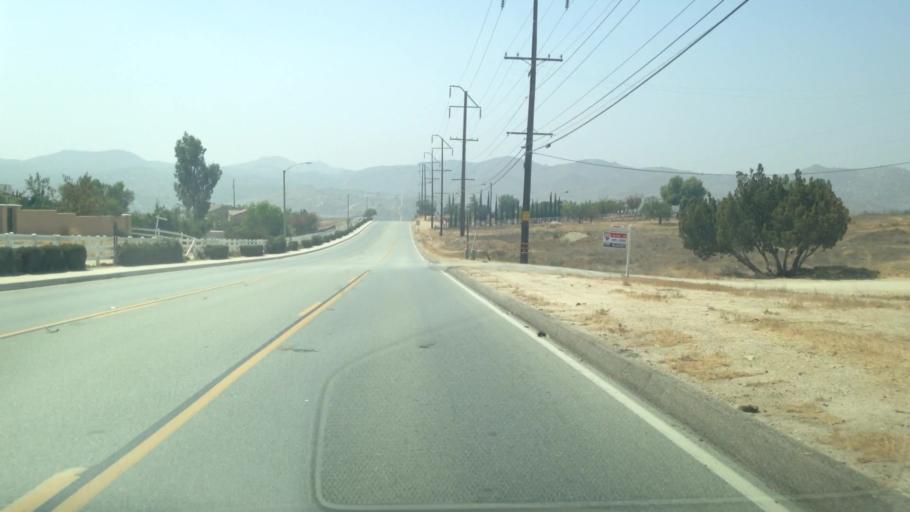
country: US
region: California
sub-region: Riverside County
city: Mead Valley
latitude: 33.8474
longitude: -117.3312
